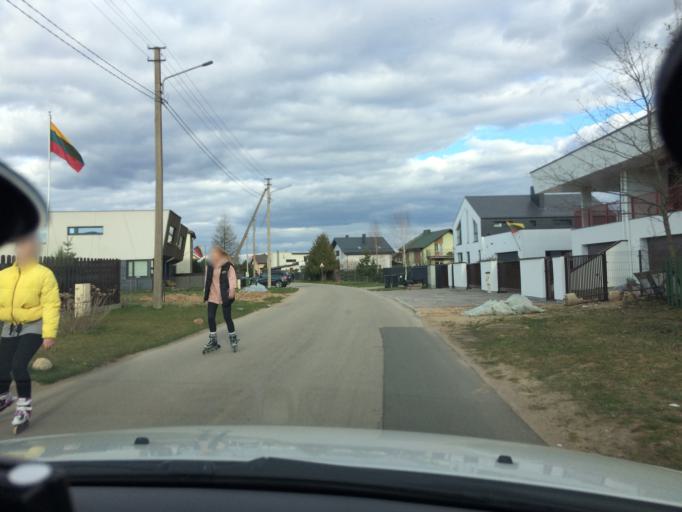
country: LT
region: Vilnius County
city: Rasos
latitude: 54.7749
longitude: 25.3498
